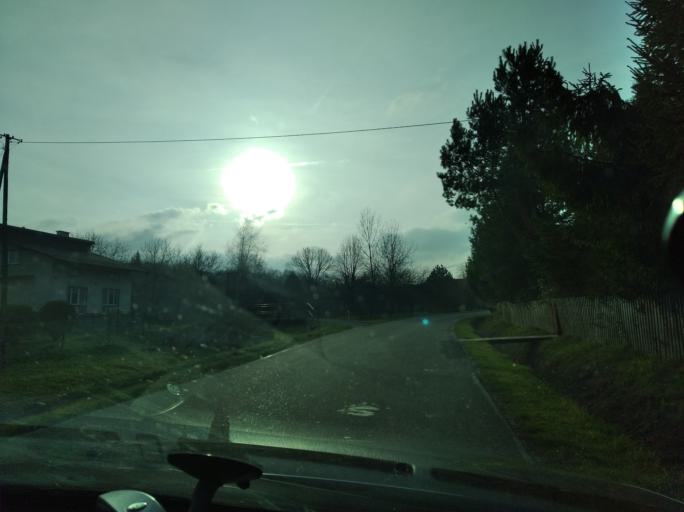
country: PL
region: Subcarpathian Voivodeship
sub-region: Powiat przeworski
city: Lopuszka Wielka
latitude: 49.9386
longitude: 22.3991
